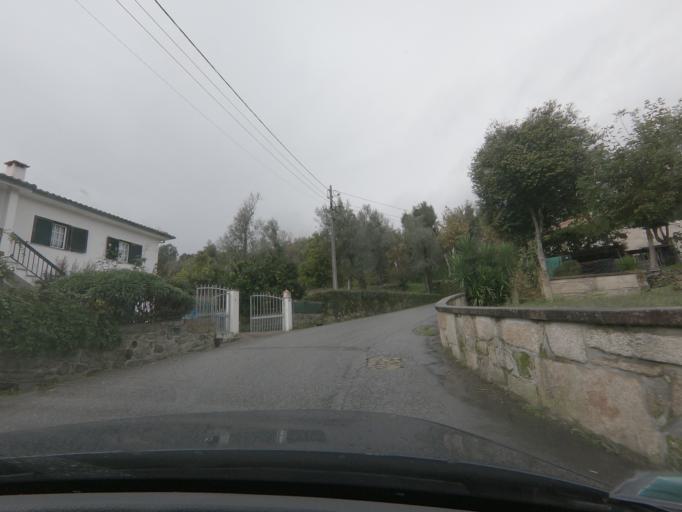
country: PT
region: Vila Real
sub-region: Mondim de Basto
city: Mondim de Basto
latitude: 41.3758
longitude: -7.9523
